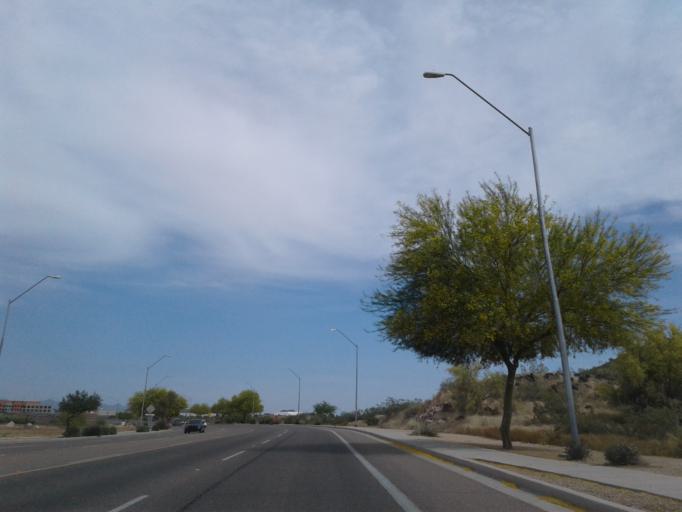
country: US
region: Arizona
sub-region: Maricopa County
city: Peoria
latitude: 33.7001
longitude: -112.1212
